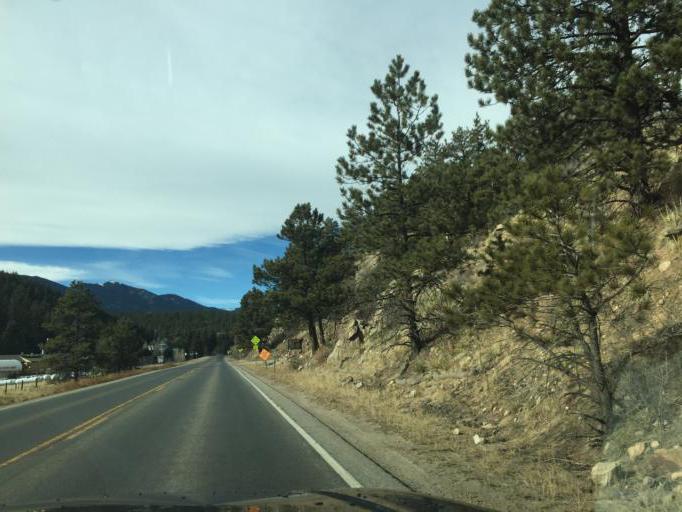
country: US
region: Colorado
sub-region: Jefferson County
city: Evergreen
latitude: 39.4071
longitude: -105.4853
